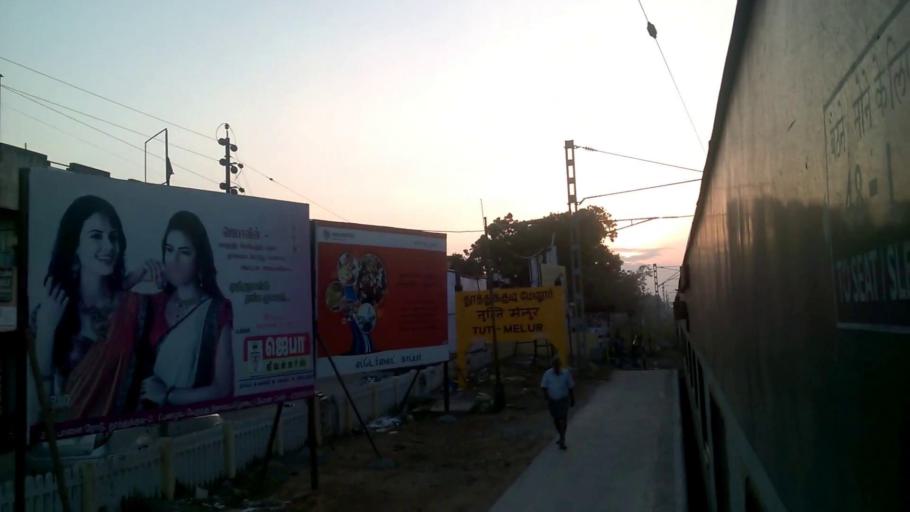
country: IN
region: Tamil Nadu
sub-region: Thoothukkudi
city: Korampallam
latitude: 8.8079
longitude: 78.1478
